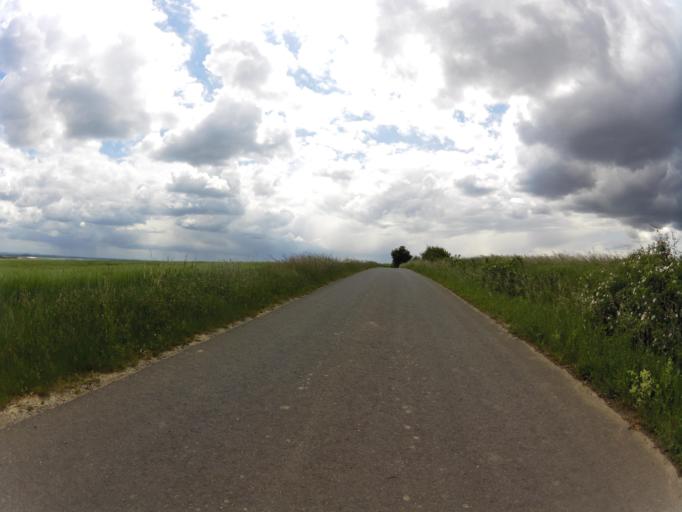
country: DE
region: Bavaria
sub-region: Regierungsbezirk Unterfranken
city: Guntersleben
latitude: 49.8798
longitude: 9.8791
